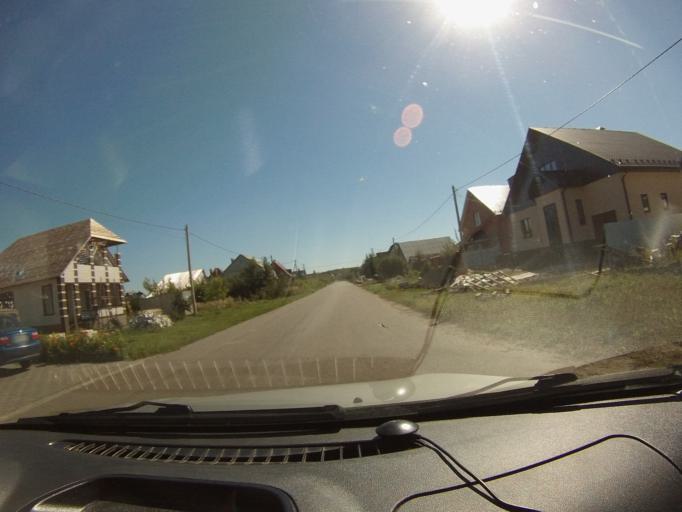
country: RU
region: Tambov
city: Komsomolets
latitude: 52.7649
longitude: 41.3628
